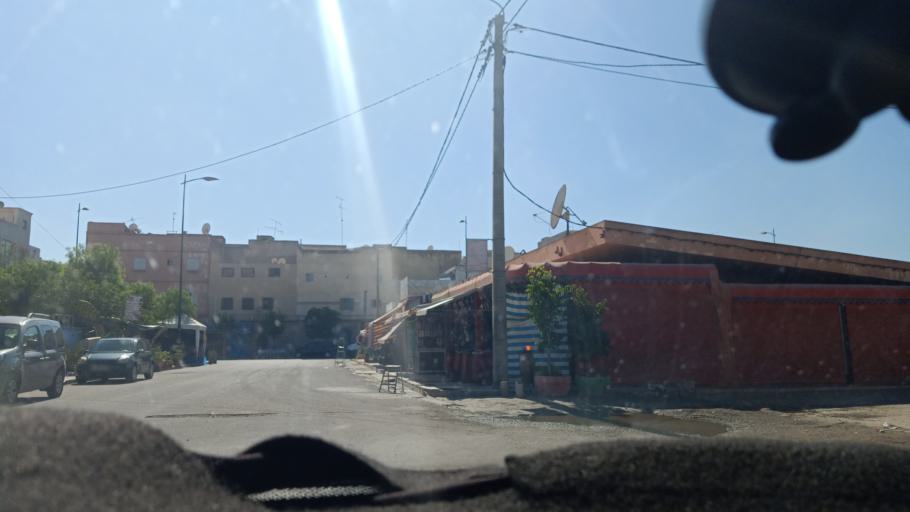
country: MA
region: Doukkala-Abda
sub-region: Safi
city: Youssoufia
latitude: 32.2426
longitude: -8.5354
